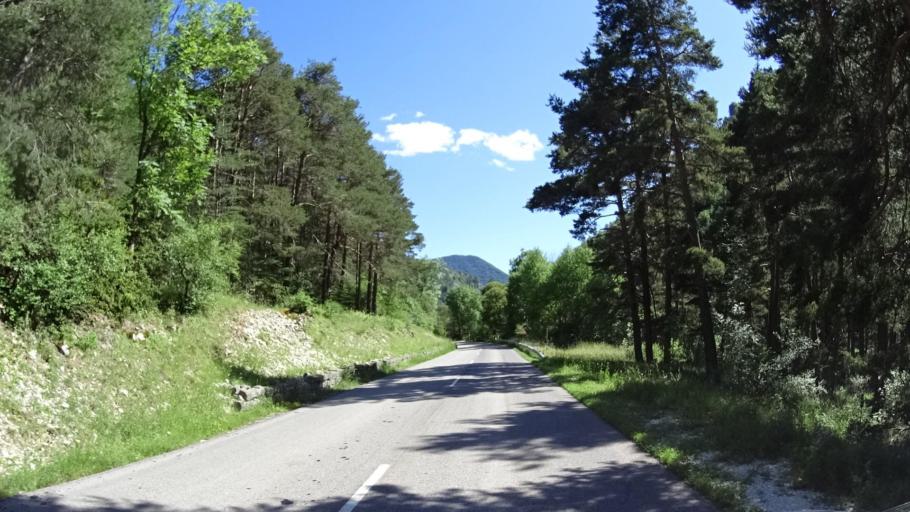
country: FR
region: Provence-Alpes-Cote d'Azur
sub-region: Departement des Alpes-de-Haute-Provence
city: Annot
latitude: 44.0657
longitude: 6.5749
